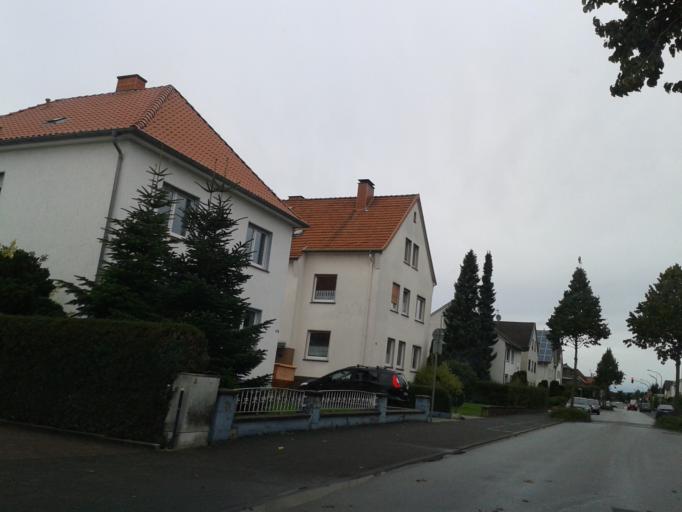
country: DE
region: North Rhine-Westphalia
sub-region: Regierungsbezirk Detmold
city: Paderborn
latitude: 51.7385
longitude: 8.7632
